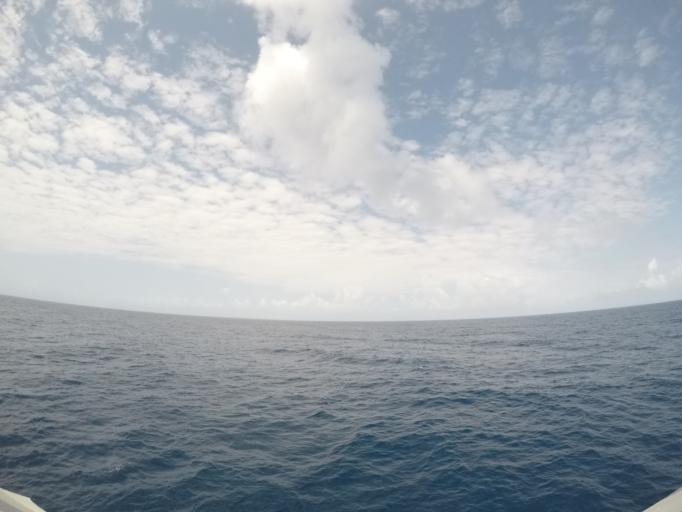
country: TZ
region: Zanzibar North
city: Nungwi
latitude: -5.5755
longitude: 39.3635
